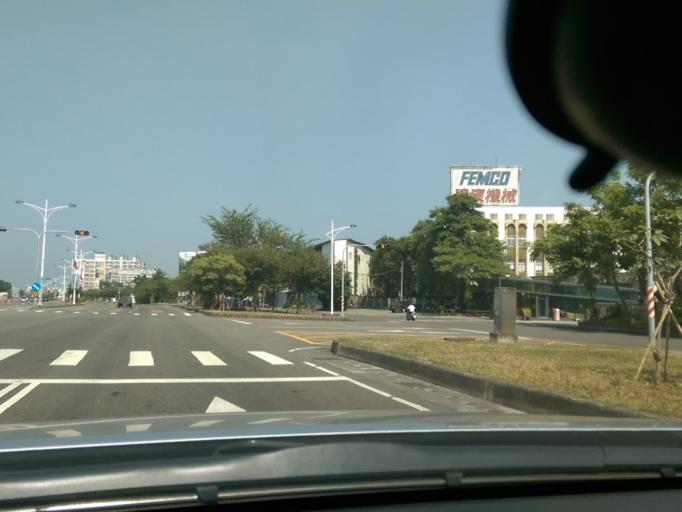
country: TW
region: Taiwan
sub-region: Chiayi
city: Jiayi Shi
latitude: 23.5084
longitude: 120.4465
